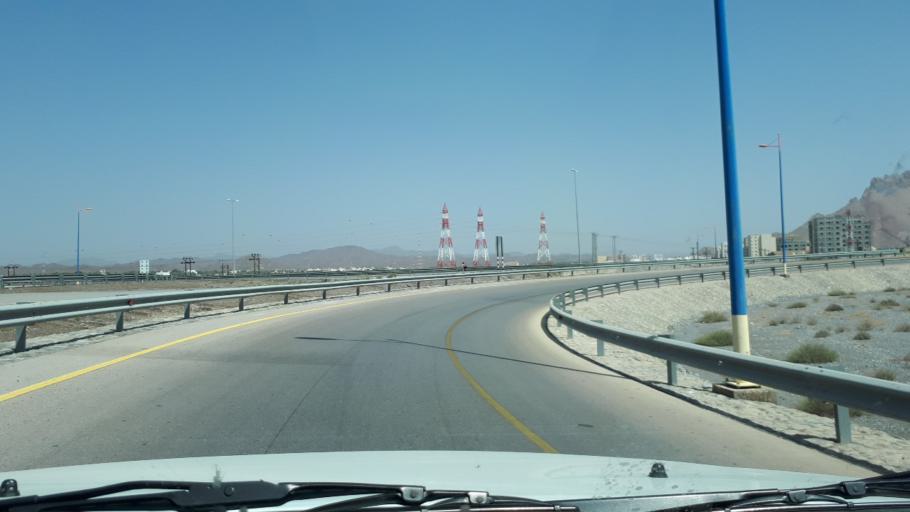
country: OM
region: Muhafazat ad Dakhiliyah
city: Nizwa
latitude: 22.8573
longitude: 57.5385
